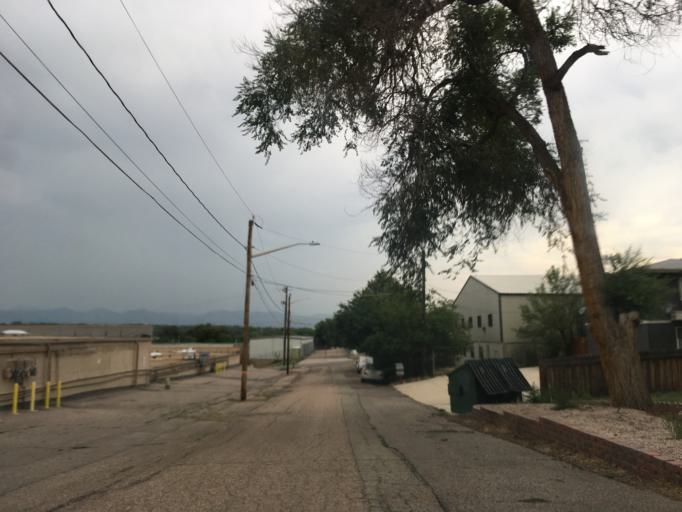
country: US
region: Colorado
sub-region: Arapahoe County
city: Sheridan
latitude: 39.6543
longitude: -105.0287
